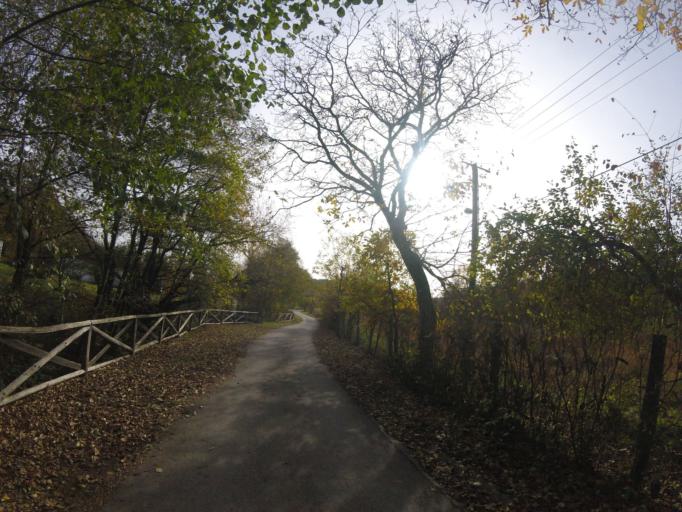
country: HU
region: Borsod-Abauj-Zemplen
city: Gonc
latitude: 48.5376
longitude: 21.4522
